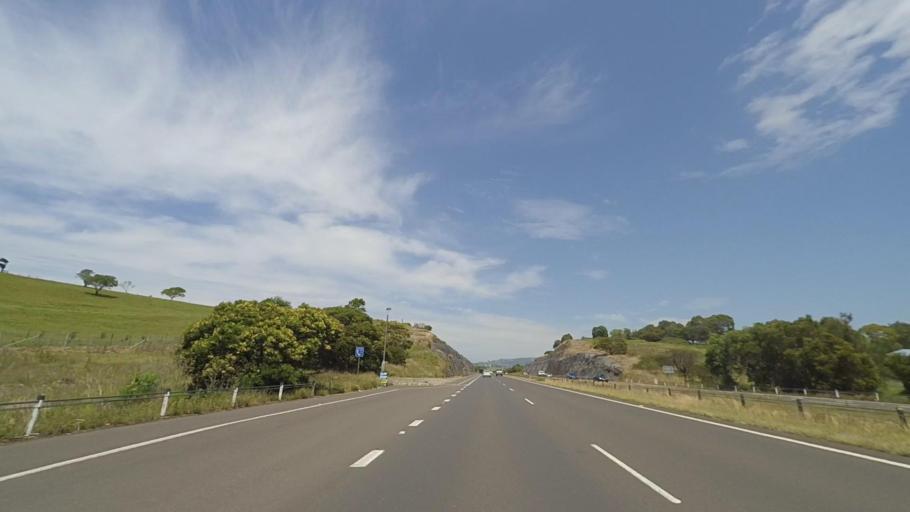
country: AU
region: New South Wales
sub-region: Shellharbour
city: Croom
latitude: -34.6213
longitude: 150.8377
